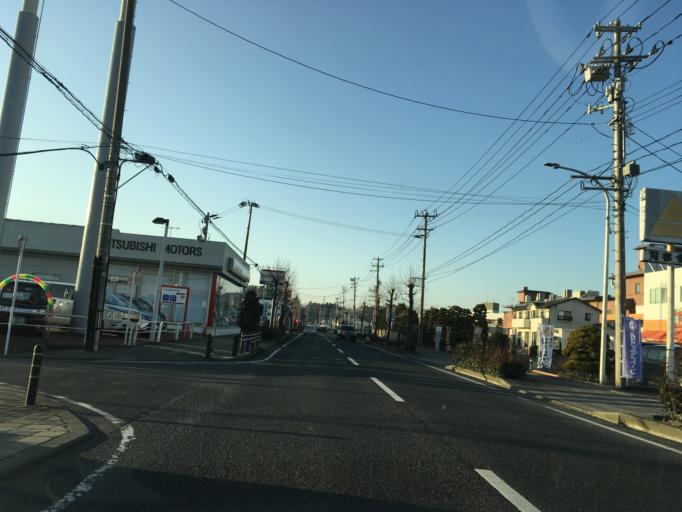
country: JP
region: Miyagi
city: Wakuya
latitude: 38.6890
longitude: 141.1840
